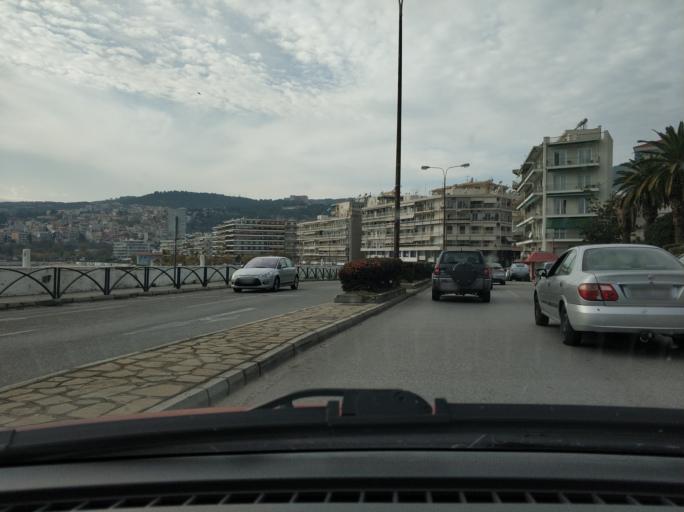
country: GR
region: East Macedonia and Thrace
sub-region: Nomos Kavalas
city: Kavala
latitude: 40.9349
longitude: 24.4008
